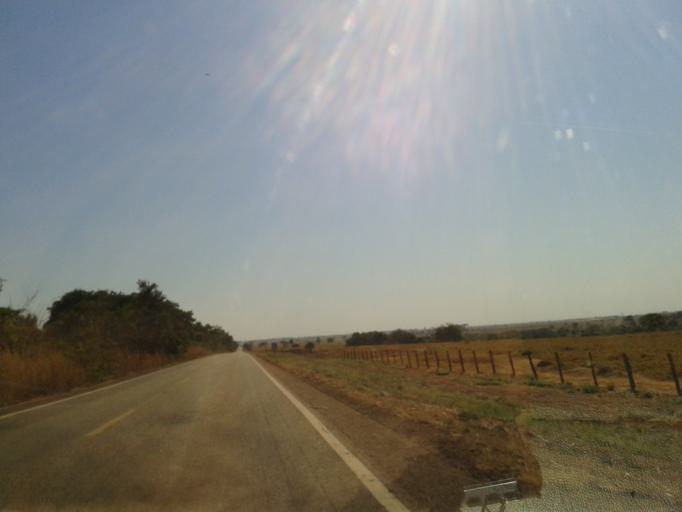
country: BR
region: Goias
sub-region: Mozarlandia
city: Mozarlandia
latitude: -14.3843
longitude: -50.4361
